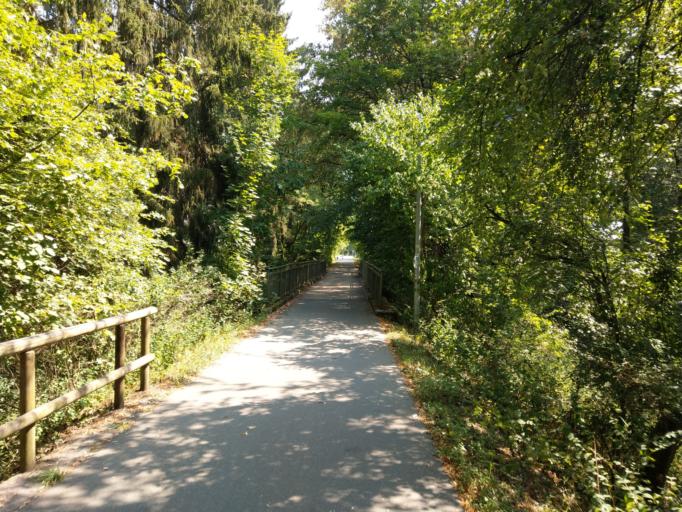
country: DE
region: Bavaria
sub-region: Upper Franconia
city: Bayreuth
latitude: 49.9306
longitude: 11.5717
